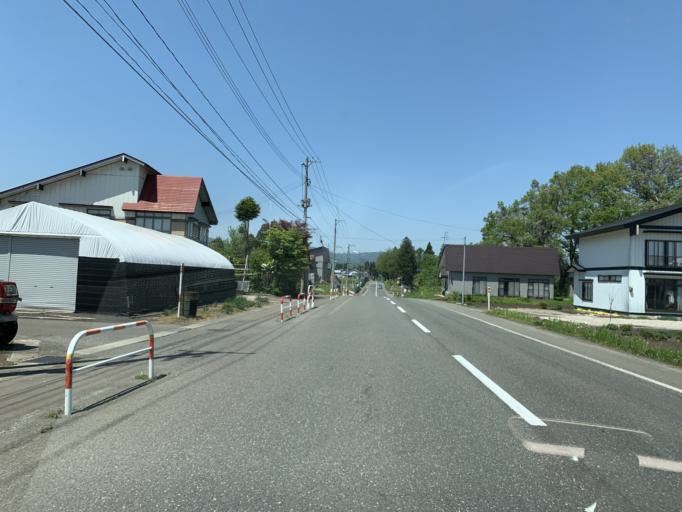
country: JP
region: Akita
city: Yokotemachi
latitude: 39.3855
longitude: 140.7582
